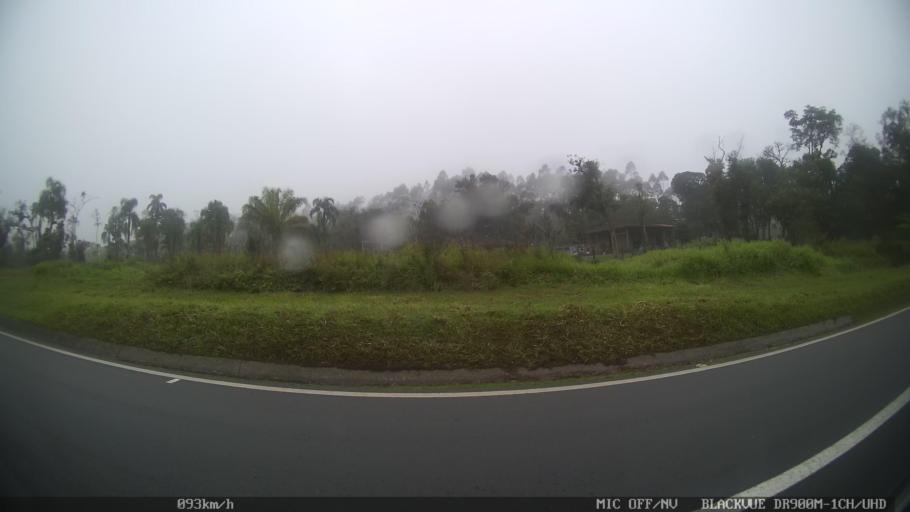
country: BR
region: Parana
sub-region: Antonina
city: Antonina
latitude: -25.1118
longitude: -48.7763
